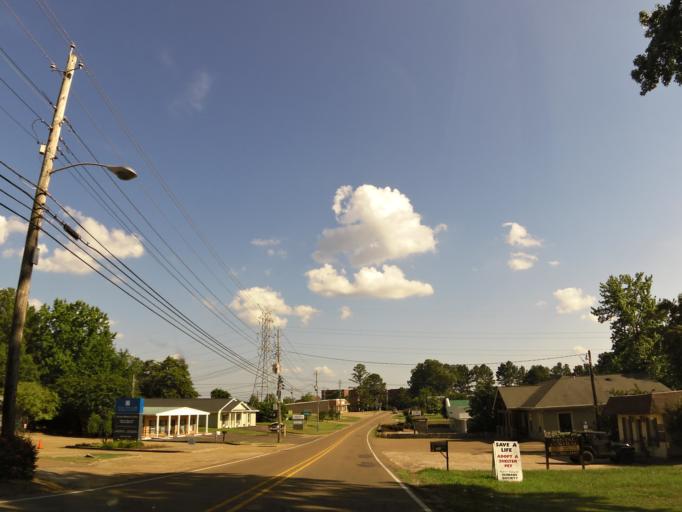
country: US
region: Mississippi
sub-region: Lafayette County
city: Oxford
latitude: 34.3519
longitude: -89.5210
